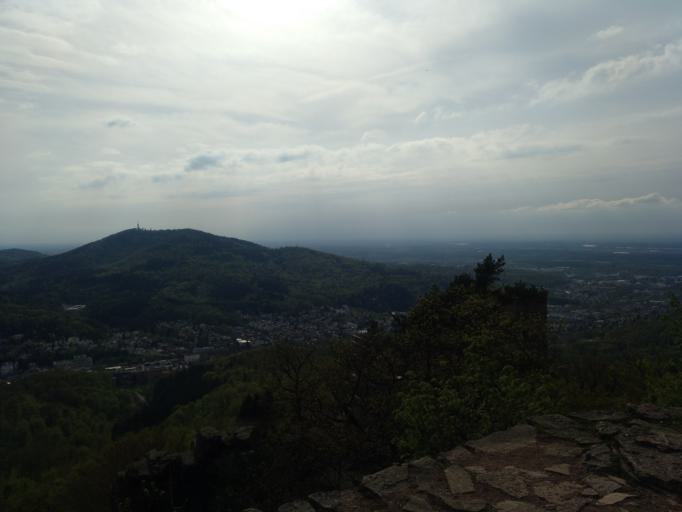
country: DE
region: Baden-Wuerttemberg
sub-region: Karlsruhe Region
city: Baden-Baden
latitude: 48.7766
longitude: 8.2463
